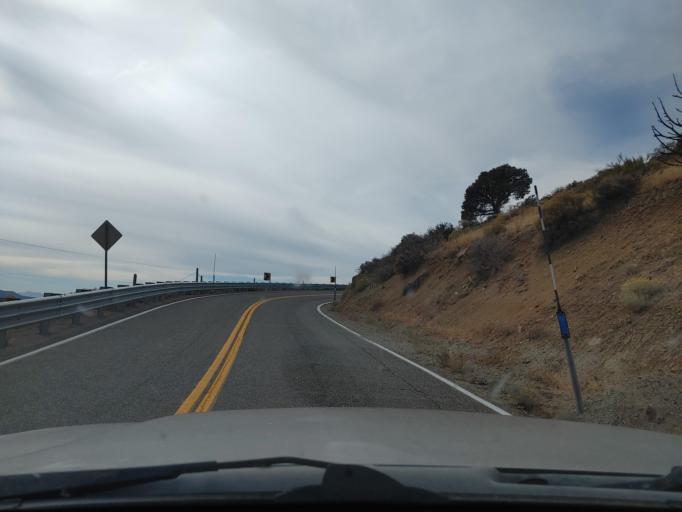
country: US
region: Nevada
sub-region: Storey County
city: Virginia City
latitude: 39.2821
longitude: -119.6283
